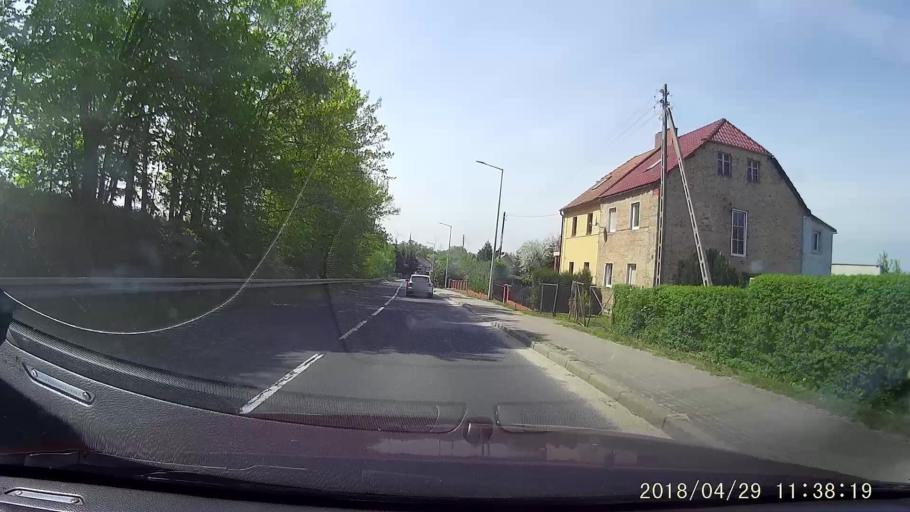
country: DE
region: Saxony
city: Ostritz
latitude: 51.0603
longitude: 14.9775
